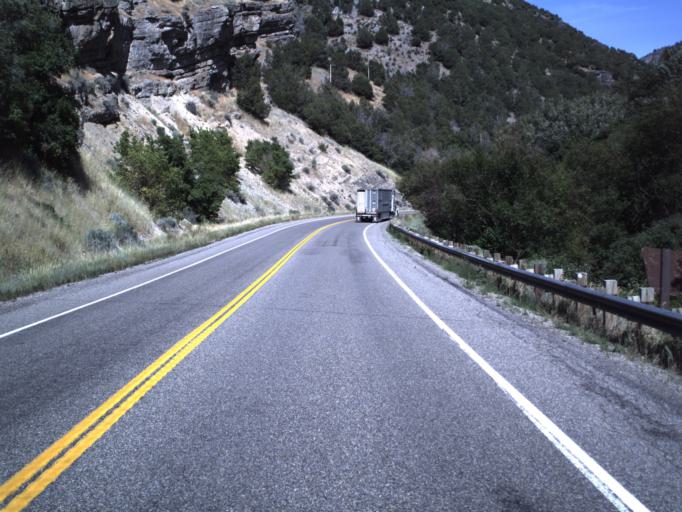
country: US
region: Utah
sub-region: Cache County
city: North Logan
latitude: 41.7654
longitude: -111.6864
